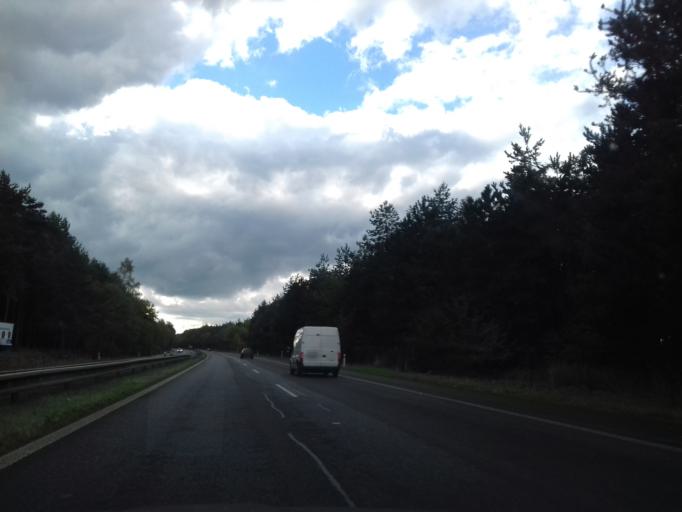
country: CZ
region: Central Bohemia
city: Benatky nad Jizerou
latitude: 50.2731
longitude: 14.8138
